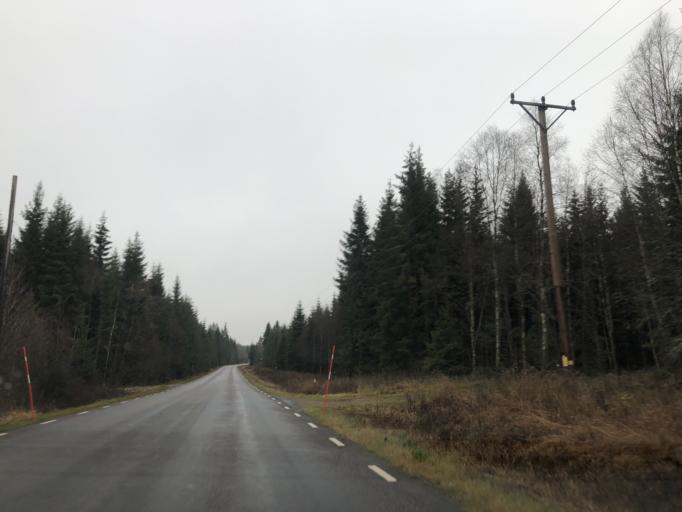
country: SE
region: Vaestra Goetaland
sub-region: Ulricehamns Kommun
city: Ulricehamn
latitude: 57.7490
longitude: 13.5241
